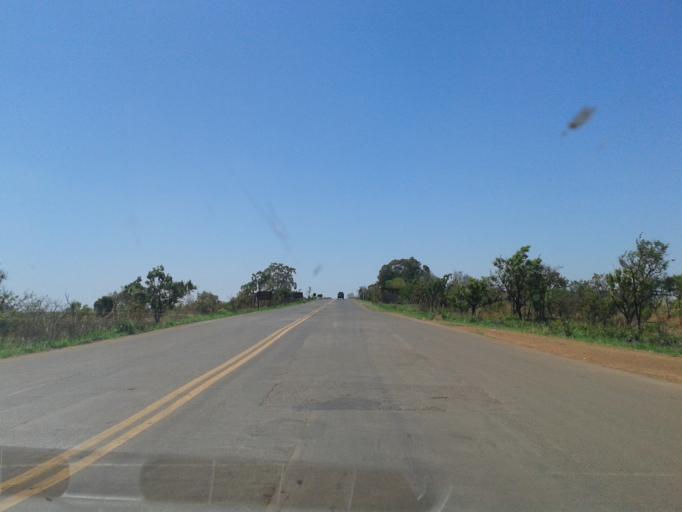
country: BR
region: Minas Gerais
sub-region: Araxa
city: Araxa
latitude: -19.4006
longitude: -47.3212
